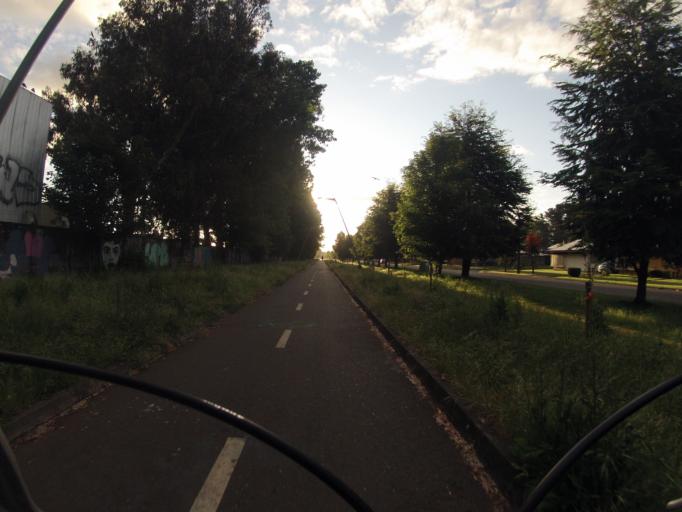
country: CL
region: Araucania
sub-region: Provincia de Cautin
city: Temuco
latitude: -38.7486
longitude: -72.6336
